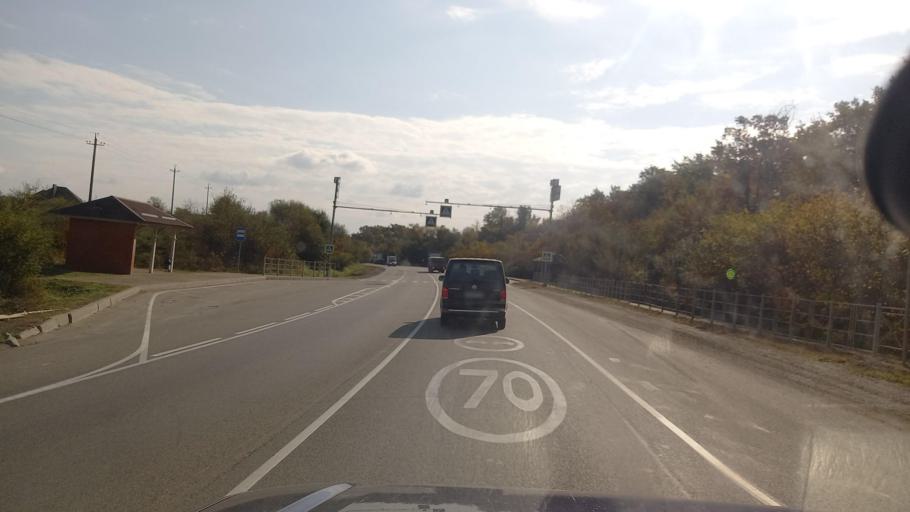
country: RU
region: Krasnodarskiy
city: Abinsk
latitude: 44.8502
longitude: 38.1362
